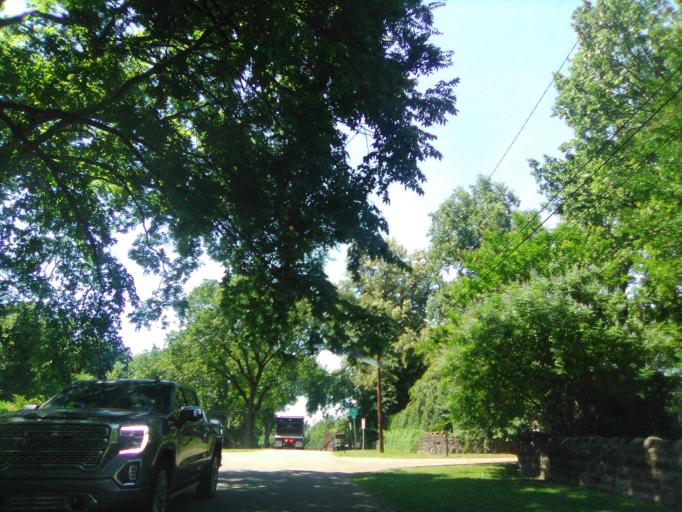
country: US
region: Tennessee
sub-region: Davidson County
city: Belle Meade
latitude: 36.1258
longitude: -86.8400
